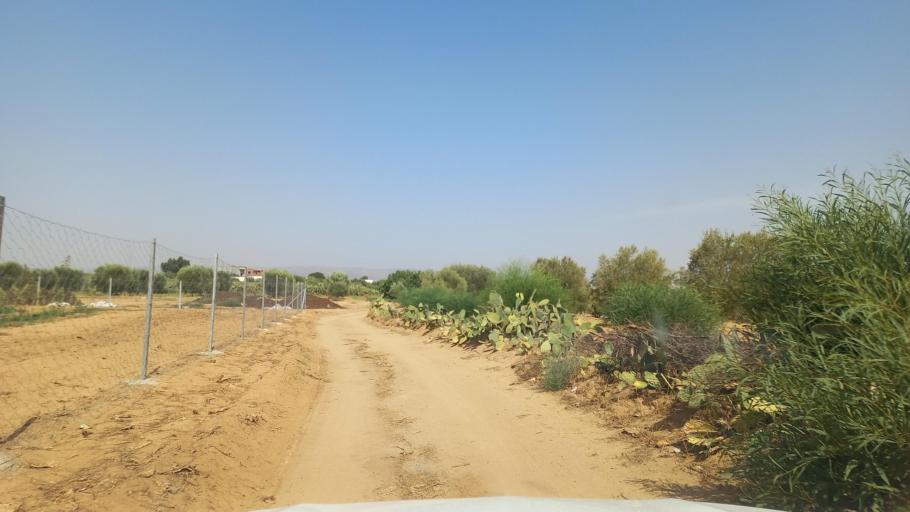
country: TN
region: Al Qasrayn
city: Kasserine
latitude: 35.2406
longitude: 9.0501
